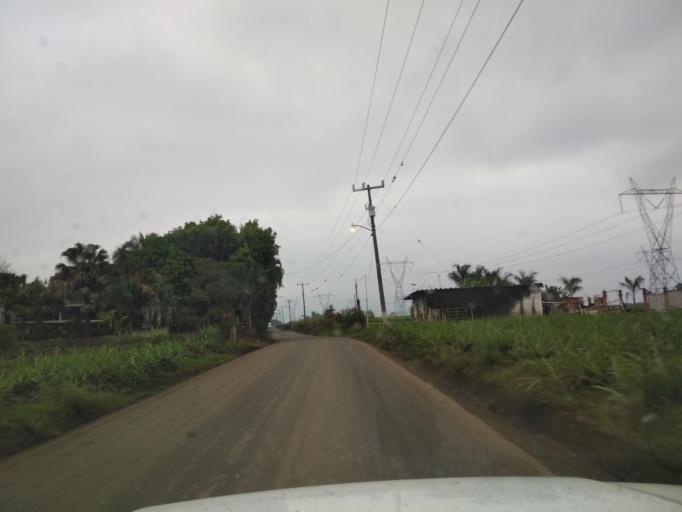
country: MX
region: Veracruz
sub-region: Cordoba
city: Veinte de Noviembre
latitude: 18.8688
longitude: -96.9636
